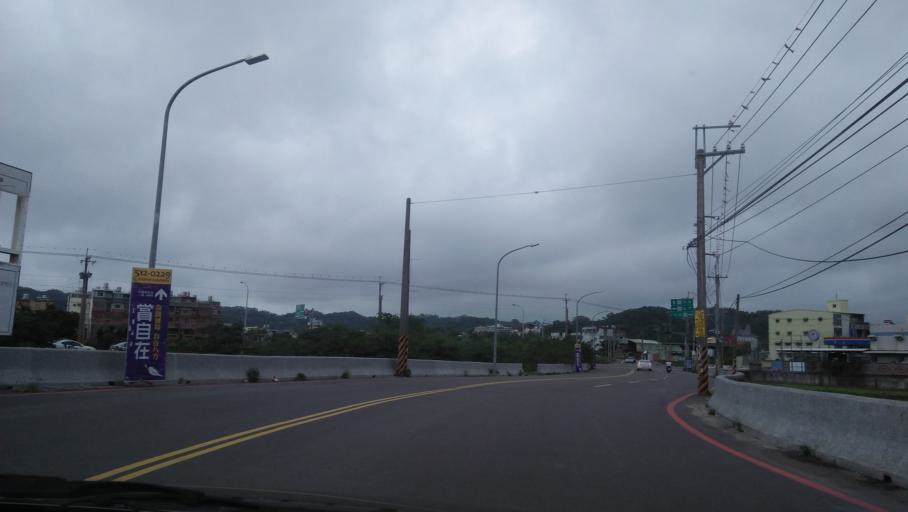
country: TW
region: Taiwan
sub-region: Hsinchu
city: Zhubei
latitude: 24.7881
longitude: 121.0627
